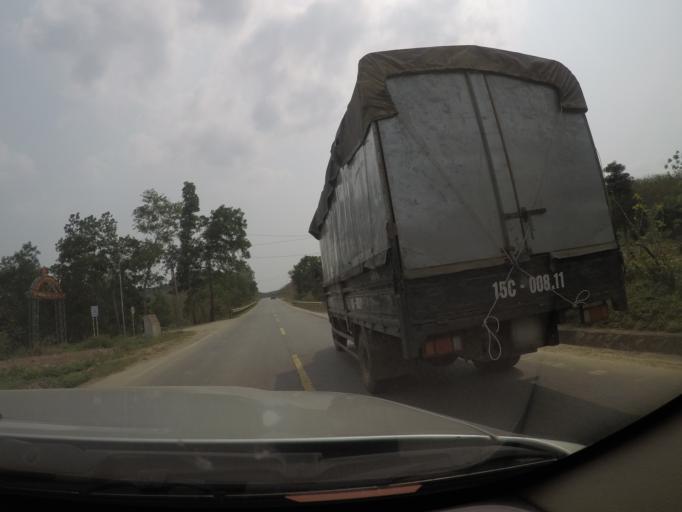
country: VN
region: Thanh Hoa
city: Thi Tran Yen Cat
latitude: 19.5103
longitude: 105.3927
